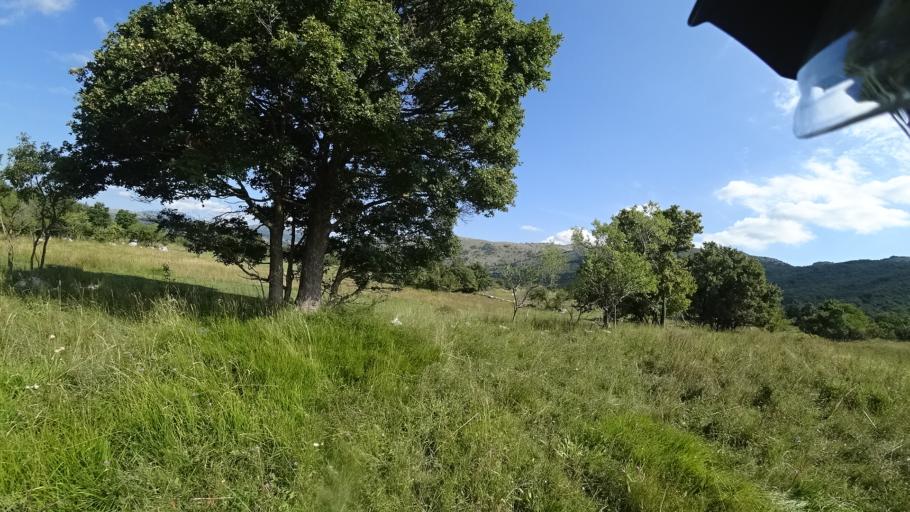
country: HR
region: Zadarska
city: Gracac
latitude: 44.3341
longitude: 15.9602
